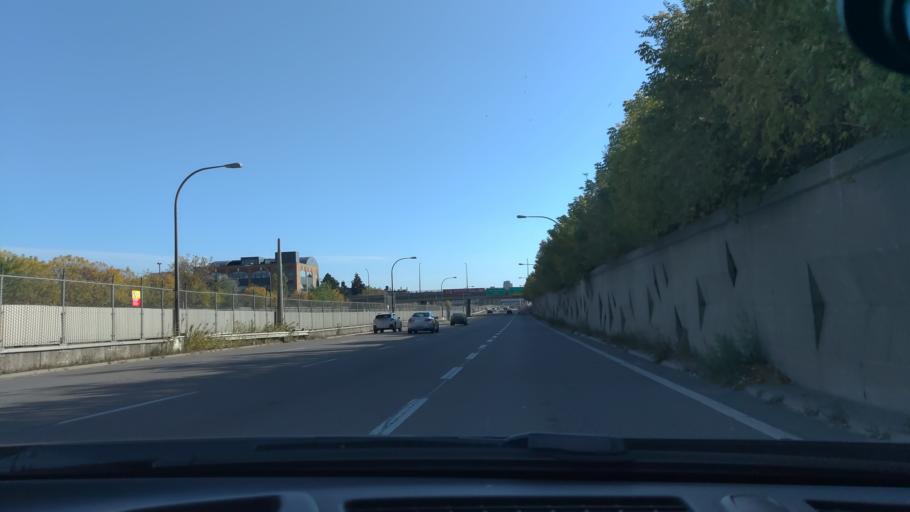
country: CA
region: Ontario
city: Toronto
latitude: 43.7211
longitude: -79.4464
